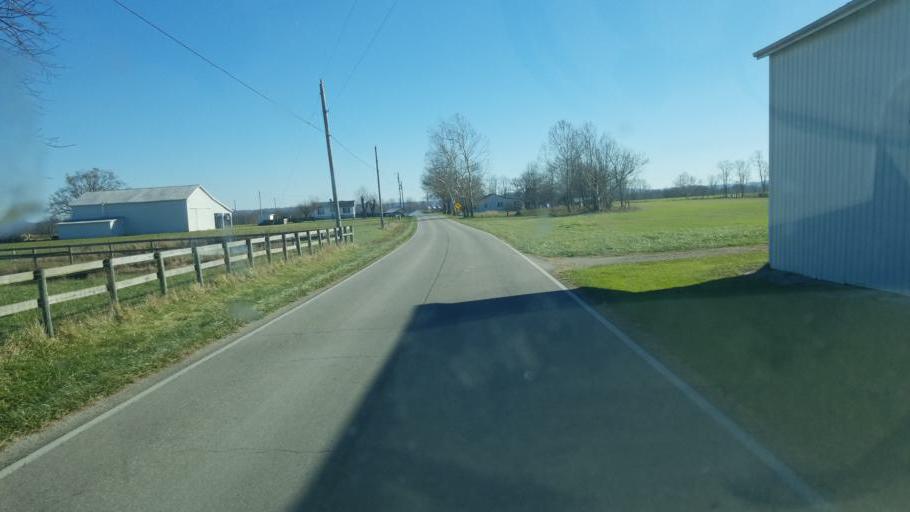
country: US
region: Ohio
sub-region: Adams County
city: Manchester
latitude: 38.5362
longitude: -83.6296
